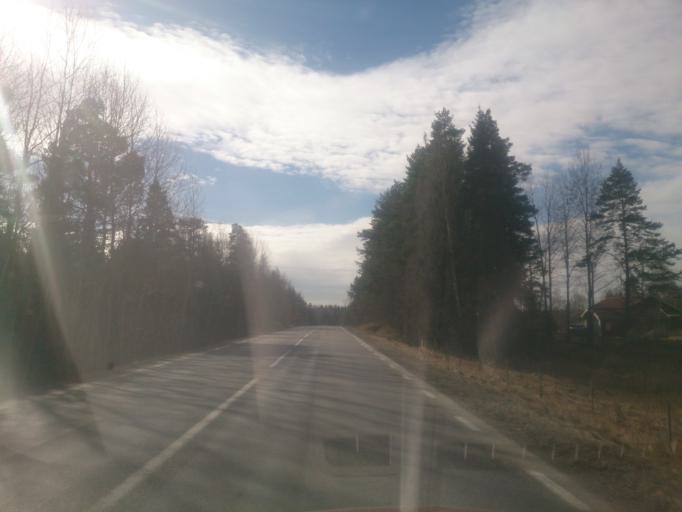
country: SE
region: OEstergoetland
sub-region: Finspangs Kommun
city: Finspang
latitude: 58.6260
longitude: 15.8206
